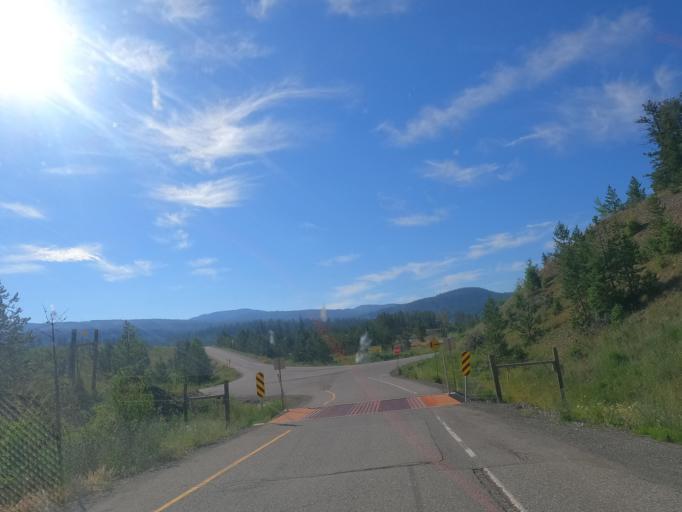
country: CA
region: British Columbia
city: Merritt
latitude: 49.8860
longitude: -120.4674
